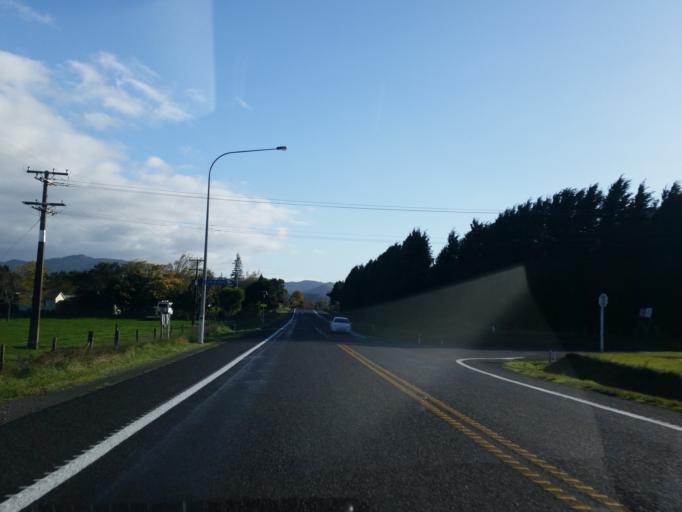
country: NZ
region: Waikato
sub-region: Hauraki District
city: Waihi
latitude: -37.4299
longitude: 175.8714
